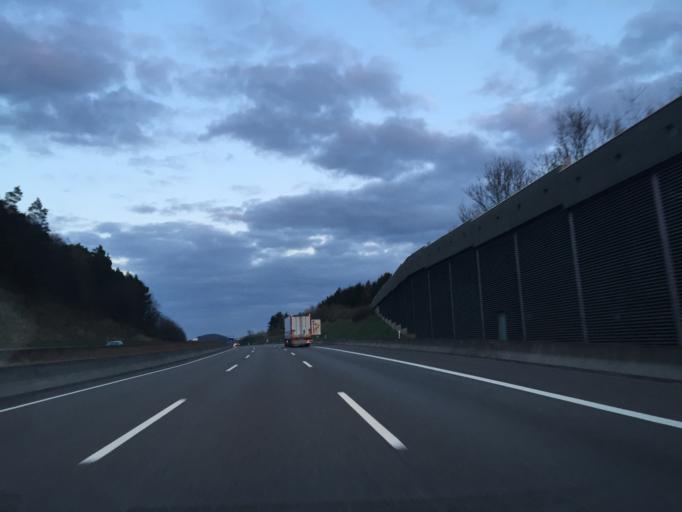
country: DE
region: Hesse
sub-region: Regierungsbezirk Kassel
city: Herleshausen
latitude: 51.0099
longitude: 10.1635
